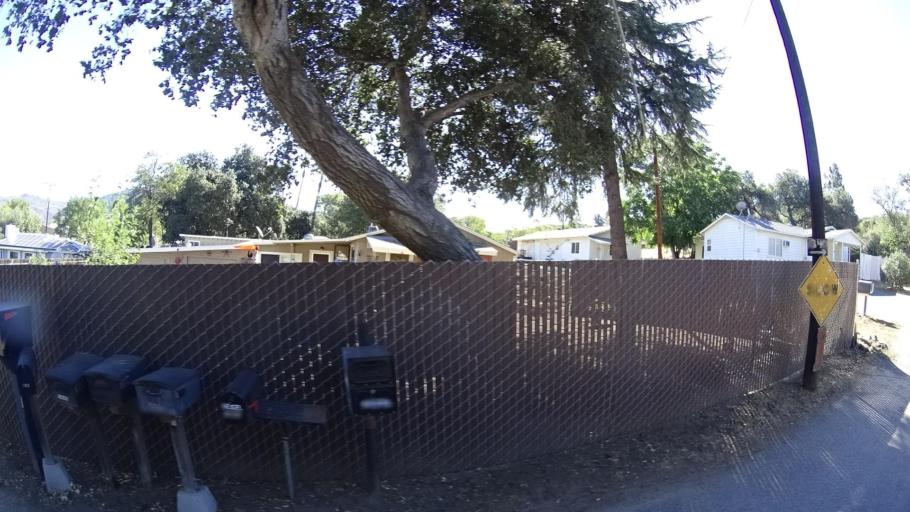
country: US
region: California
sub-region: San Diego County
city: Alpine
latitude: 32.8400
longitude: -116.6957
